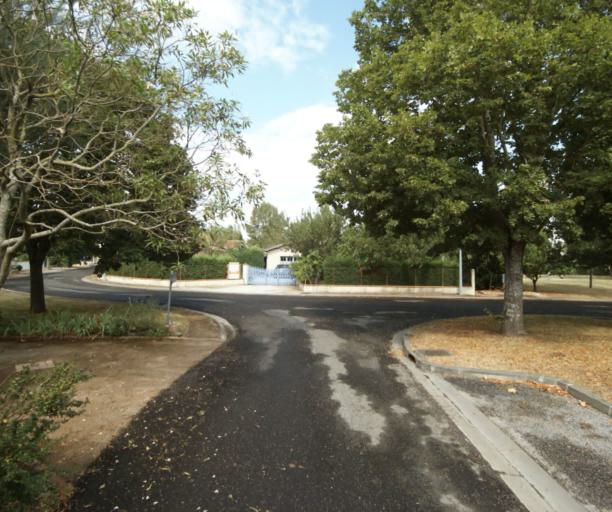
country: FR
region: Midi-Pyrenees
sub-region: Departement de la Haute-Garonne
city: Revel
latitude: 43.4602
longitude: 1.9937
